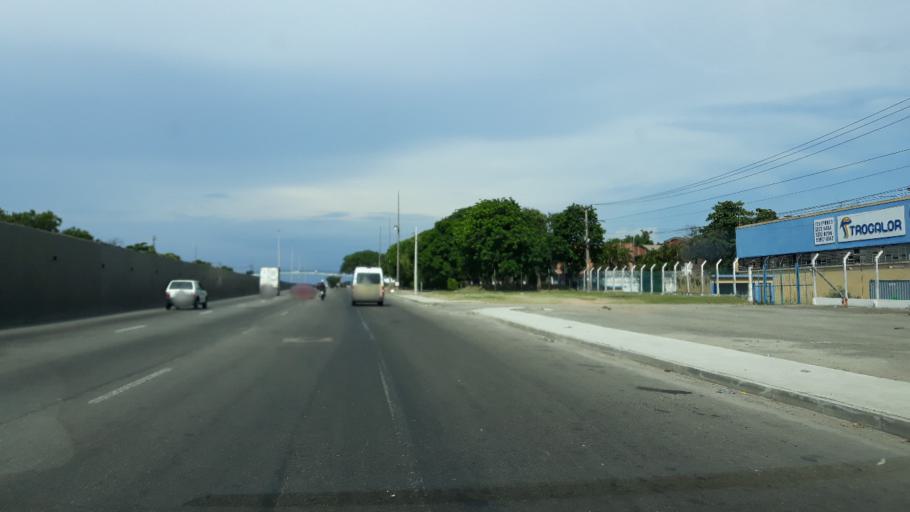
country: BR
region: Rio de Janeiro
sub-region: Sao Joao De Meriti
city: Sao Joao de Meriti
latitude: -22.8323
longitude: -43.3539
